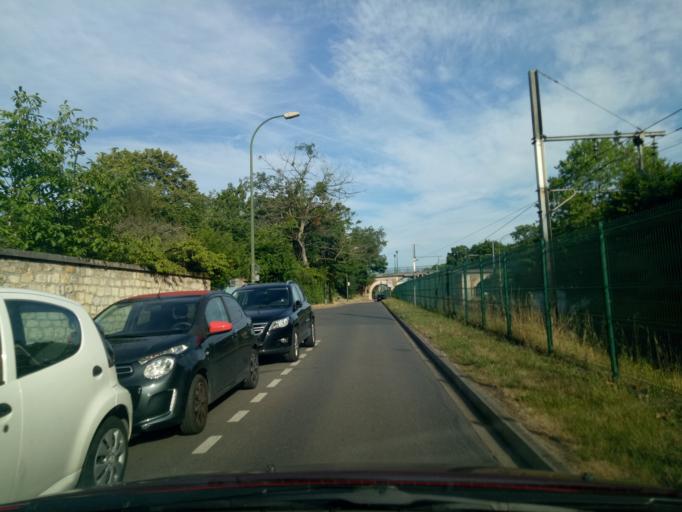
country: FR
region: Ile-de-France
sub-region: Departement des Yvelines
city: Croissy-sur-Seine
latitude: 48.8880
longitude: 2.1410
